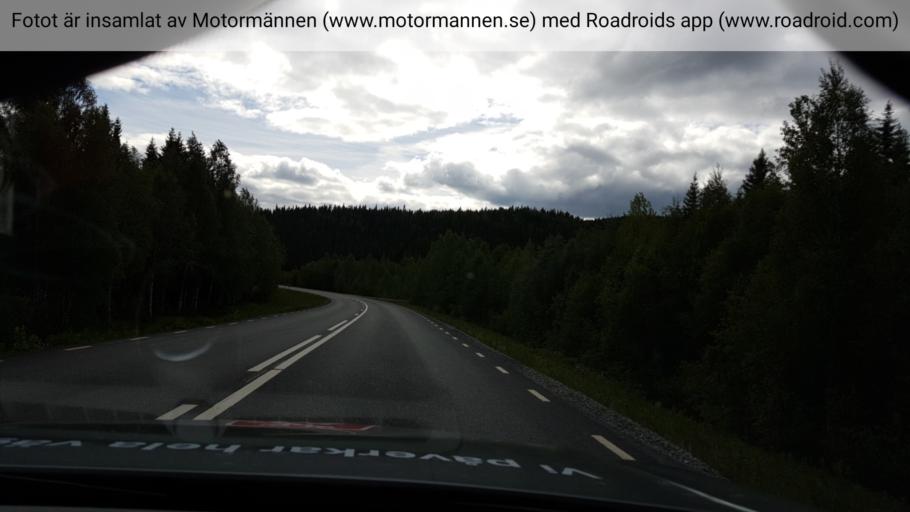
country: SE
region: Jaemtland
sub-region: Stroemsunds Kommun
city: Stroemsund
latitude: 64.1033
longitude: 15.5888
